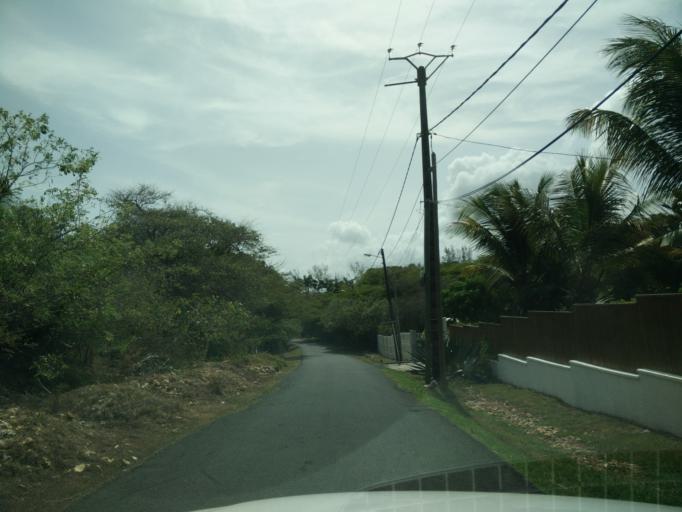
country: GP
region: Guadeloupe
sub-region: Guadeloupe
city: Sainte-Anne
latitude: 16.2433
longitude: -61.3360
